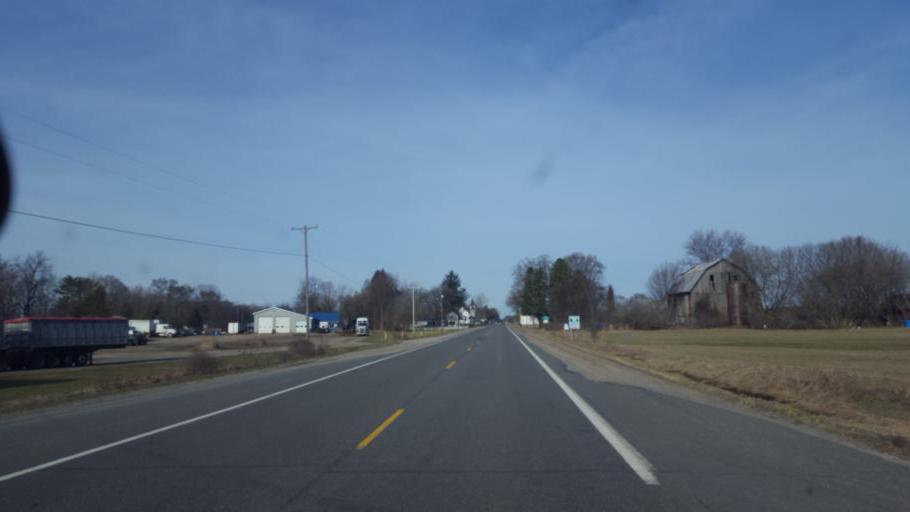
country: US
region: Michigan
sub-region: Montcalm County
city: Howard City
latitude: 43.4316
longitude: -85.3829
